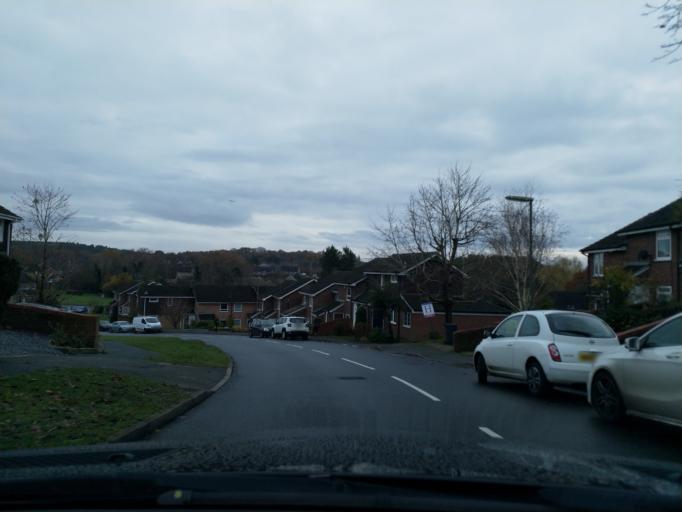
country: GB
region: England
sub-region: Surrey
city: Frimley
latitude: 51.3135
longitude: -0.7300
